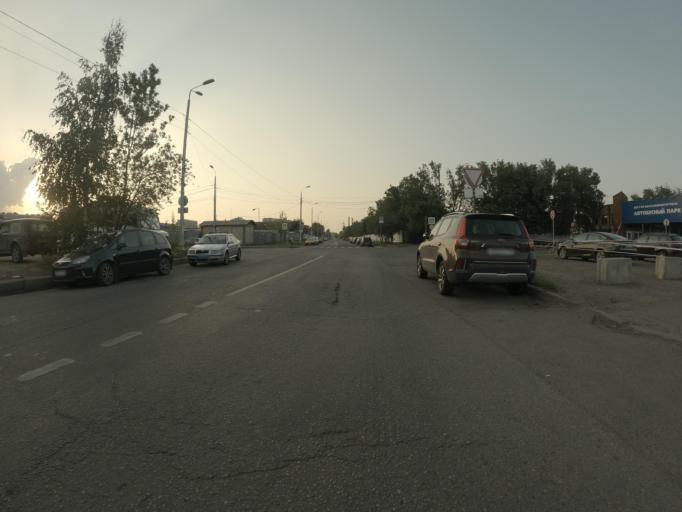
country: RU
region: St.-Petersburg
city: Krasnogvargeisky
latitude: 59.9681
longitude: 30.4411
